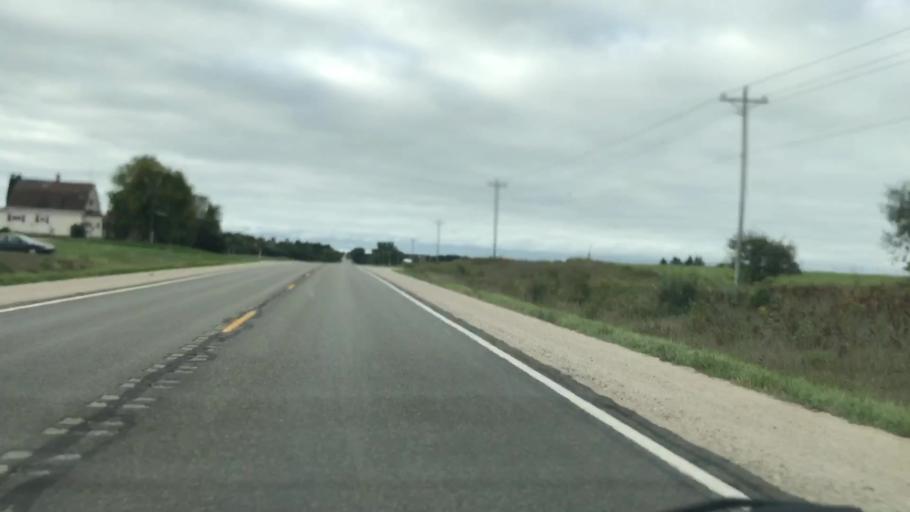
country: US
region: Michigan
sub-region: Luce County
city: Newberry
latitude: 46.1648
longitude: -85.5713
